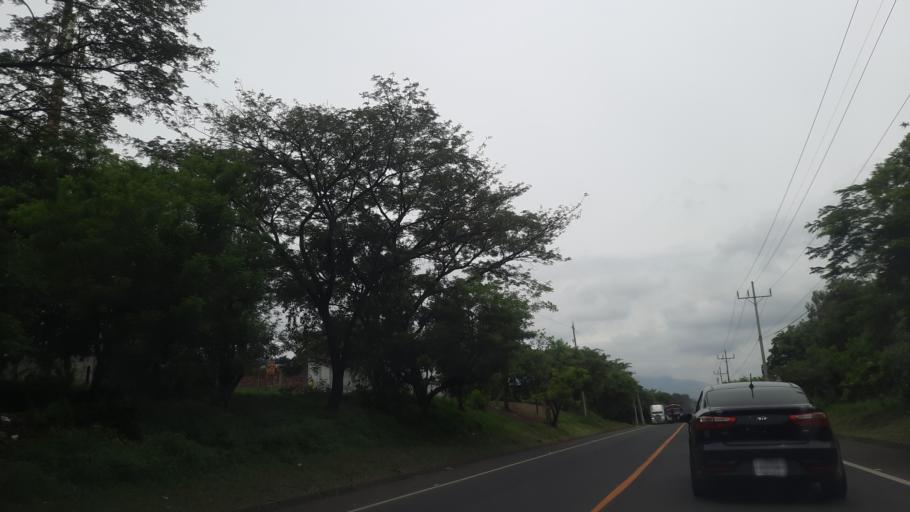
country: SV
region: Santa Ana
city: Santa Ana
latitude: 13.9881
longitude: -89.5442
